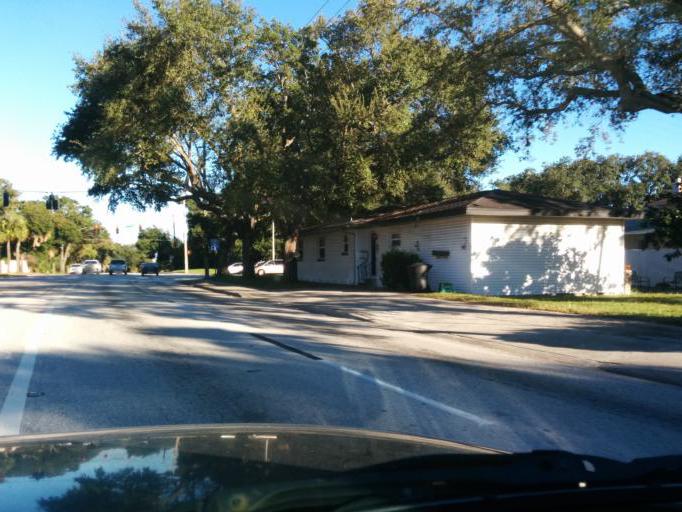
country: US
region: Florida
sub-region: Pinellas County
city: Lealman
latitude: 27.8070
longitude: -82.6475
